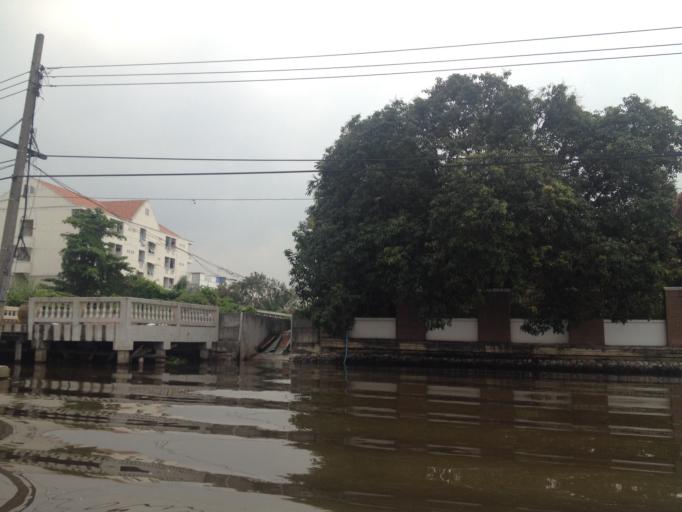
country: TH
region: Nonthaburi
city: Bang Kruai
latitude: 13.8040
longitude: 100.4735
